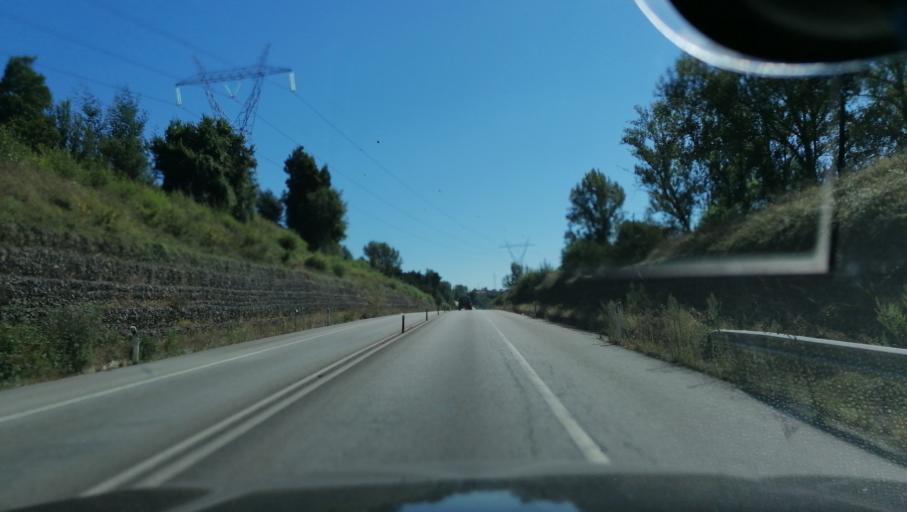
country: PT
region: Aveiro
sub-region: Oliveira de Azemeis
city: Oliveira de Azemeis
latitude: 40.8213
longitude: -8.4710
